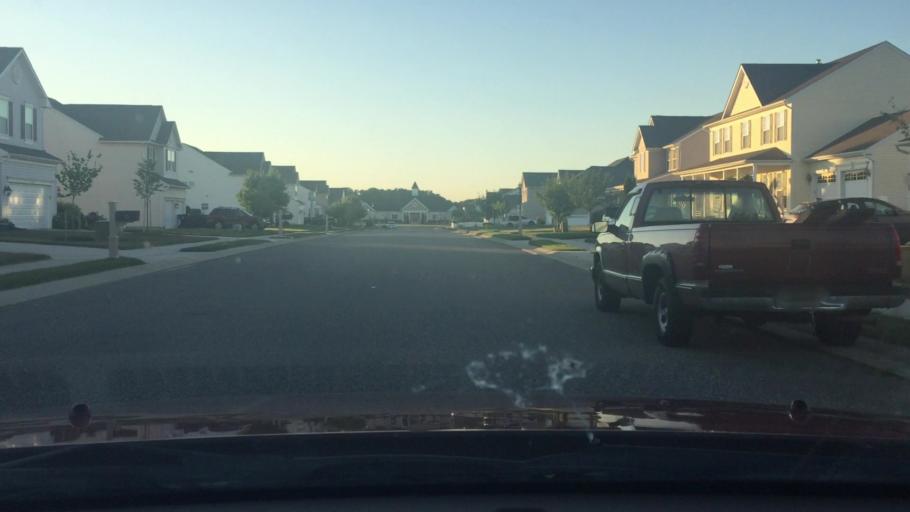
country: US
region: Delaware
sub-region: Kent County
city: Woodside East
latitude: 39.0529
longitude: -75.5223
